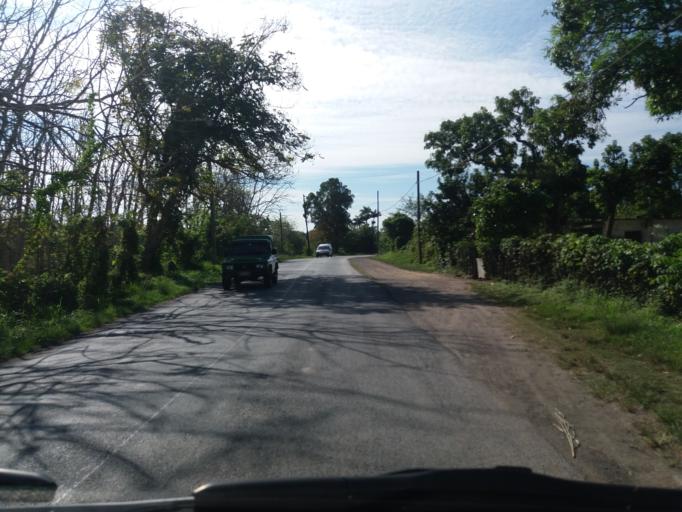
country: CU
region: Cienfuegos
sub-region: Municipio de Cienfuegos
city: Cienfuegos
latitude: 22.1648
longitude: -80.3687
